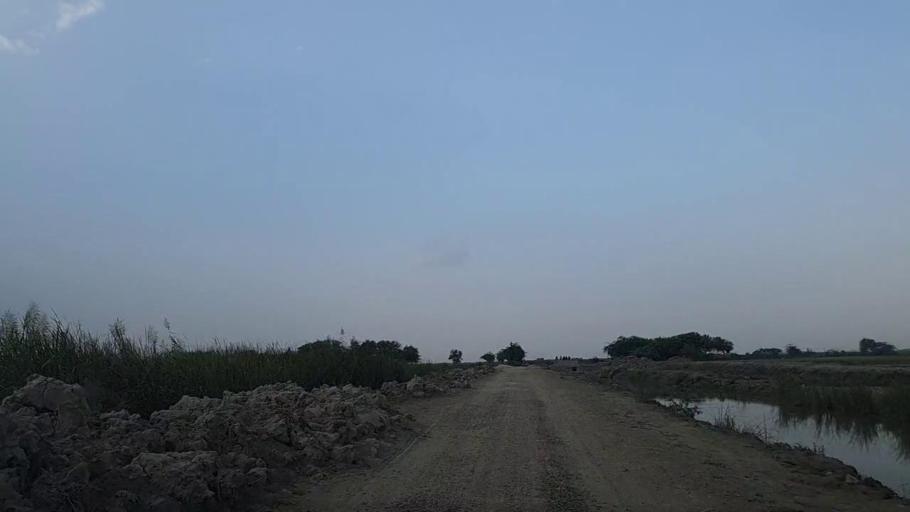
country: PK
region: Sindh
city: Daro Mehar
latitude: 24.7761
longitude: 68.1332
